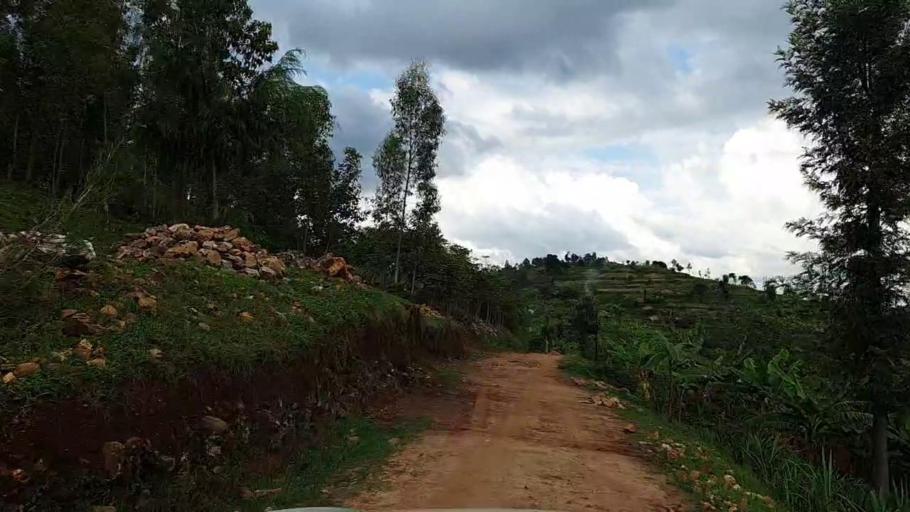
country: RW
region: Southern Province
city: Gikongoro
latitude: -2.4340
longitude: 29.6377
